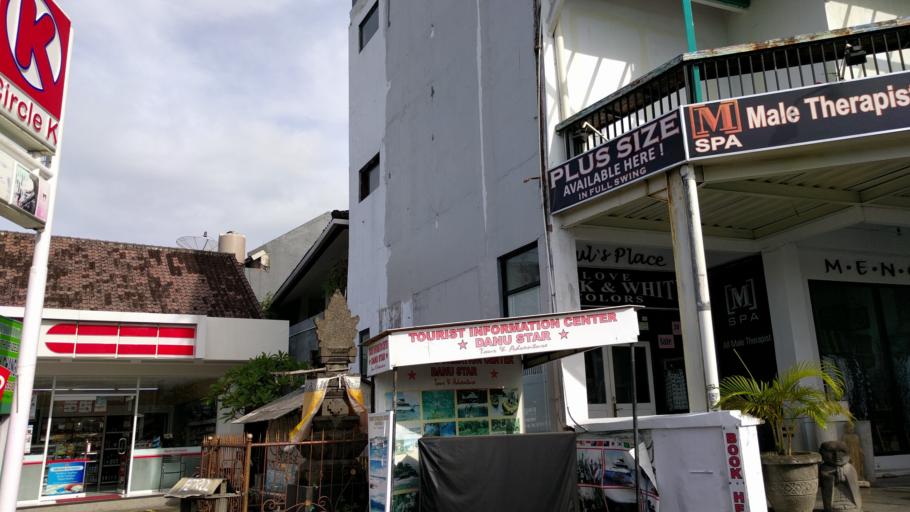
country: ID
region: Bali
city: Kuta
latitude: -8.6858
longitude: 115.1560
